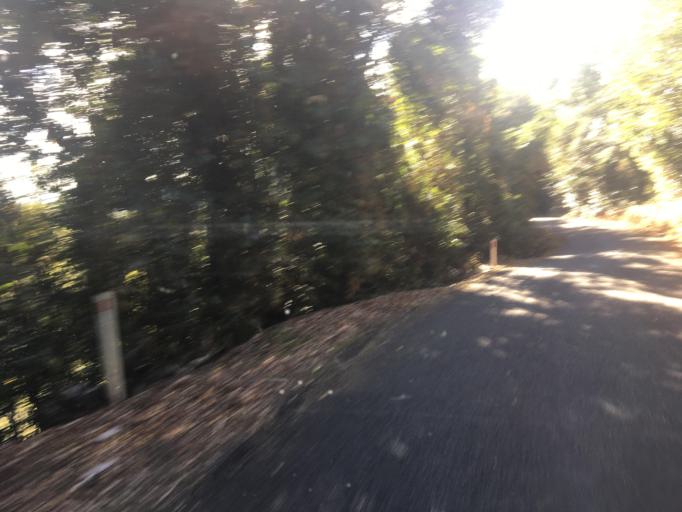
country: AU
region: Queensland
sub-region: Tablelands
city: Ravenshoe
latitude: -17.5896
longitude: 145.5935
